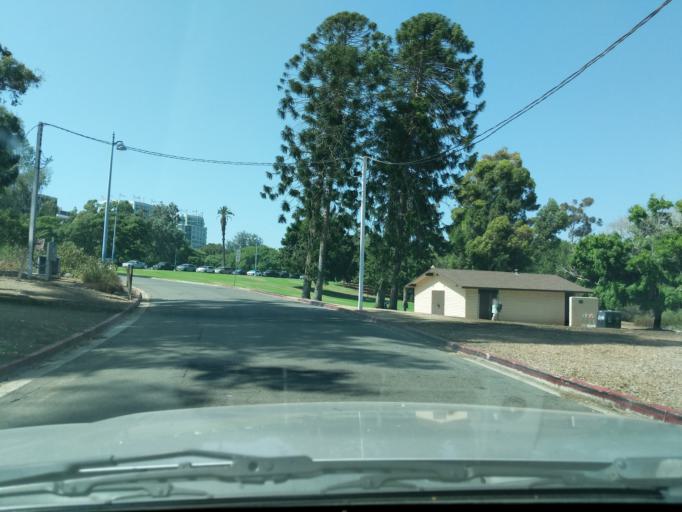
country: US
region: California
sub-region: San Diego County
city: San Diego
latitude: 32.7289
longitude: -117.1576
